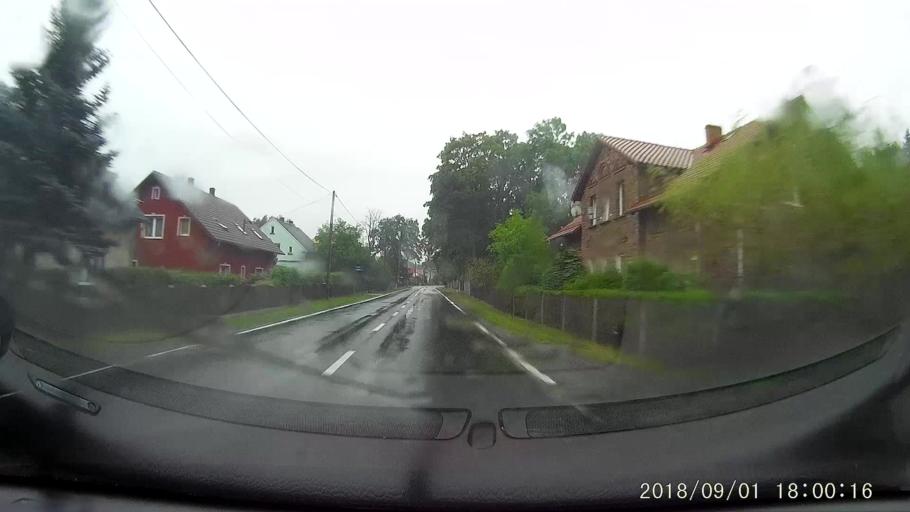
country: PL
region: Lubusz
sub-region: Powiat zaganski
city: Gozdnica
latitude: 51.4034
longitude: 15.1830
